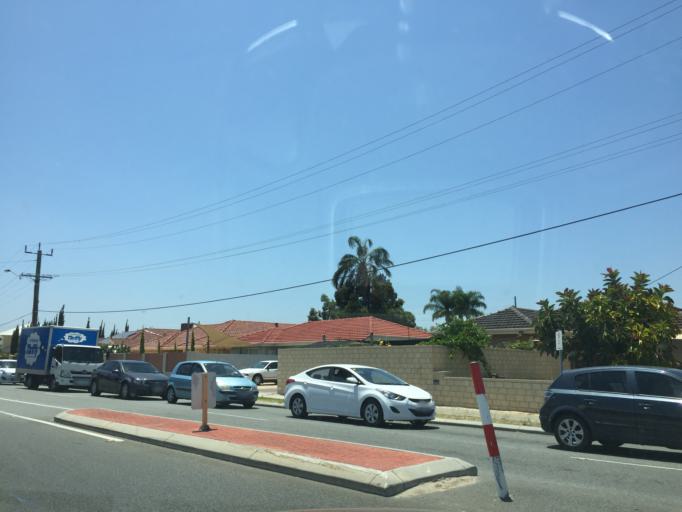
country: AU
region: Western Australia
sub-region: Canning
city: Queens Park
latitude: -32.0091
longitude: 115.9411
